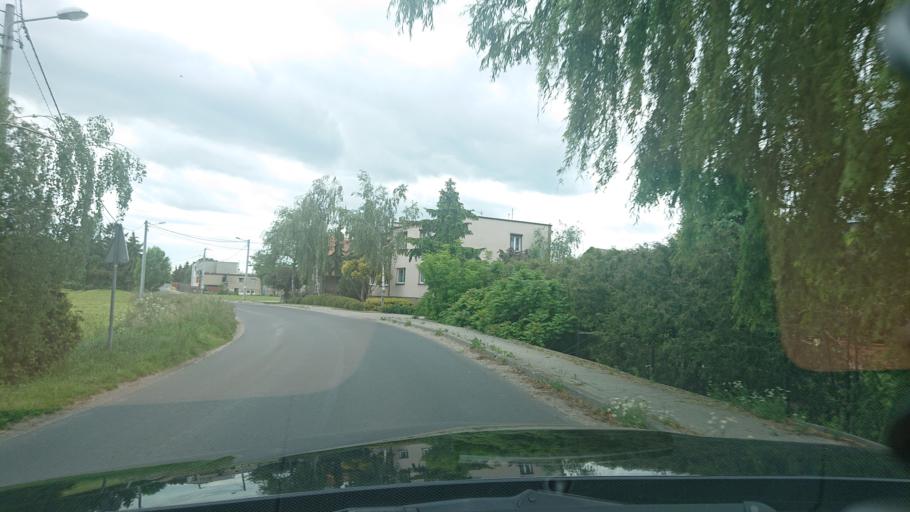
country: PL
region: Greater Poland Voivodeship
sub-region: Powiat gnieznienski
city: Gniezno
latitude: 52.5411
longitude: 17.5440
